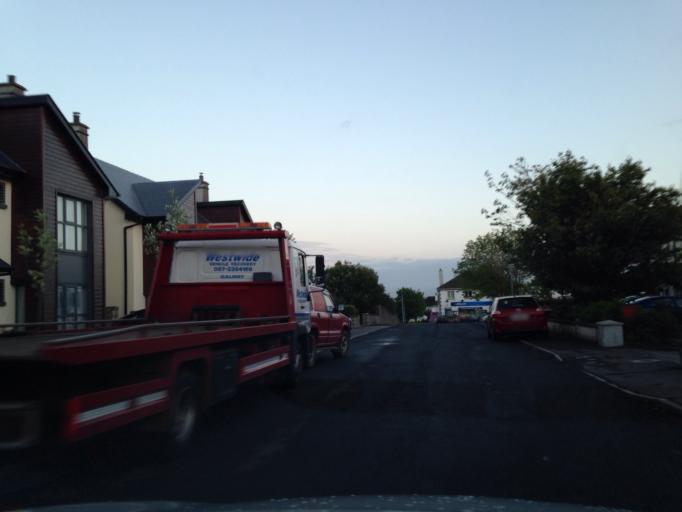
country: IE
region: Connaught
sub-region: County Galway
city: Gaillimh
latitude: 53.2738
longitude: -9.0155
